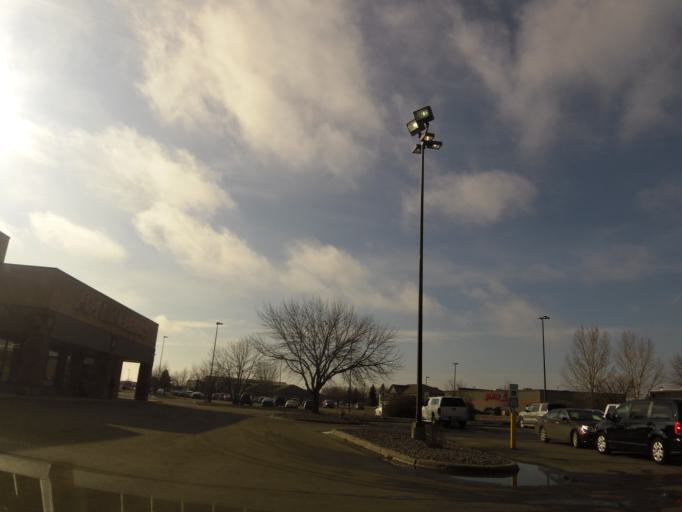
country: US
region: North Dakota
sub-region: Grand Forks County
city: Grand Forks
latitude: 47.8879
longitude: -97.0686
